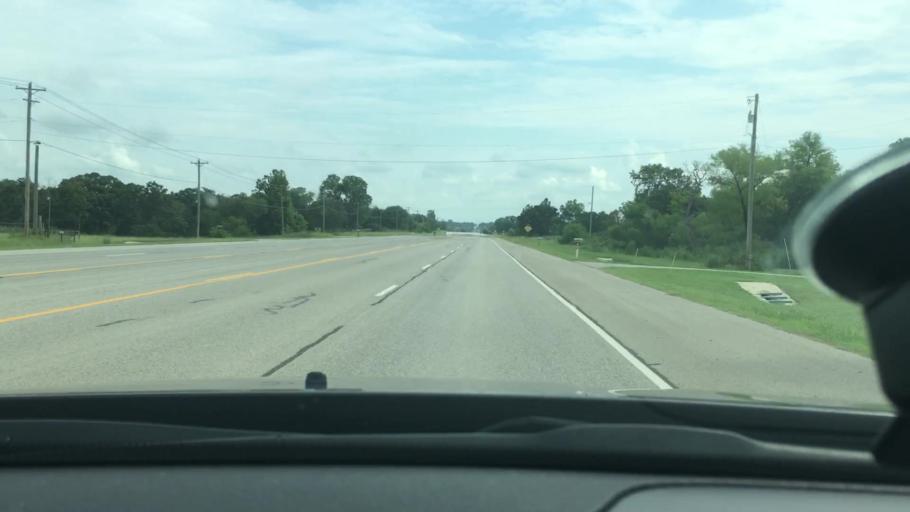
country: US
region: Oklahoma
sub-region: Carter County
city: Dickson
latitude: 34.1871
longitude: -96.9964
